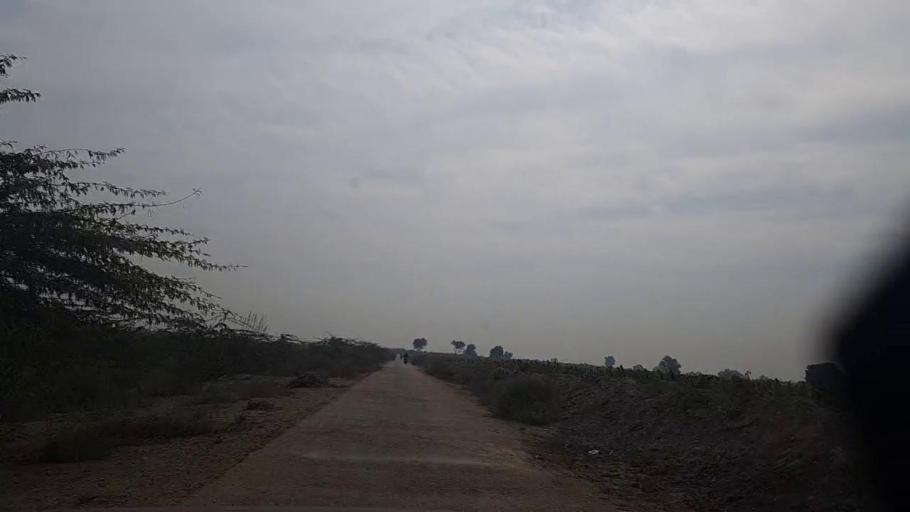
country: PK
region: Sindh
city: Sakrand
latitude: 26.2445
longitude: 68.2945
